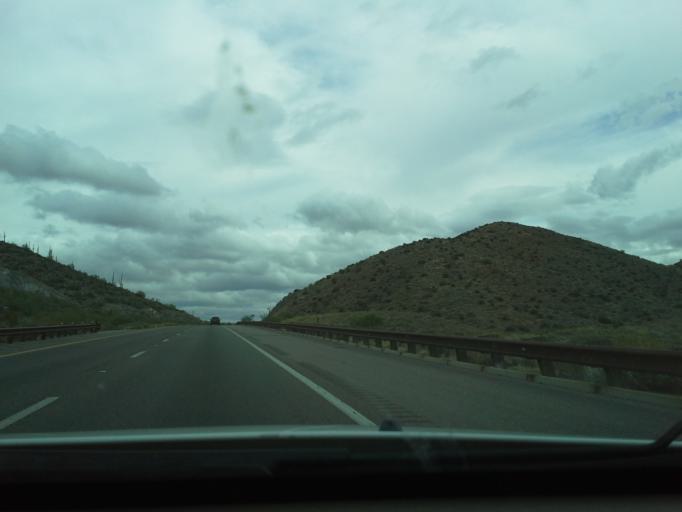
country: US
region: Arizona
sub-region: Pinal County
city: Gold Camp
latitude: 33.2738
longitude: -111.2355
